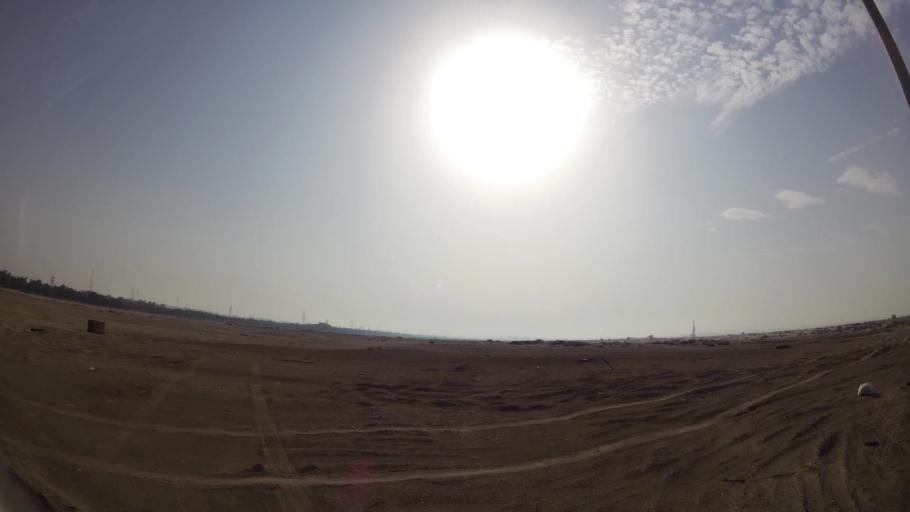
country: AE
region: Abu Dhabi
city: Abu Dhabi
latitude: 24.2622
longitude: 54.6744
